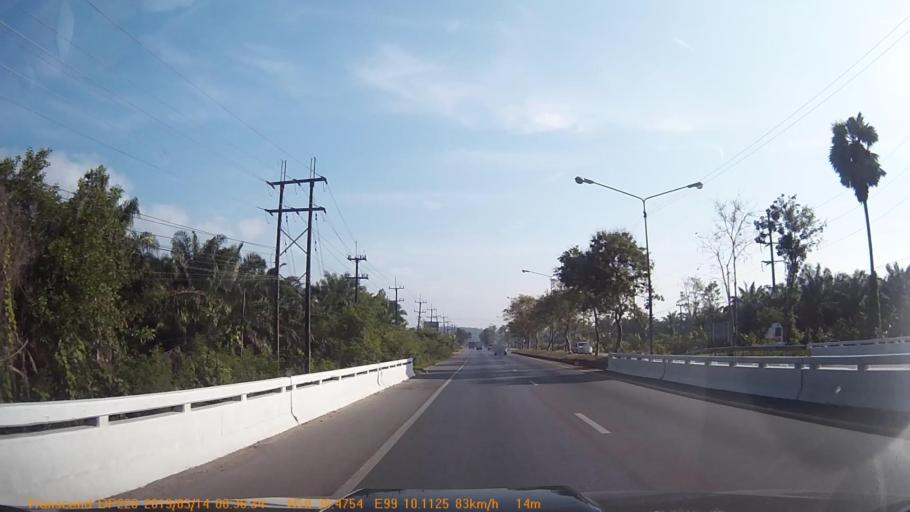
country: TH
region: Chumphon
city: Tha Sae
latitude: 10.6083
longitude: 99.1687
